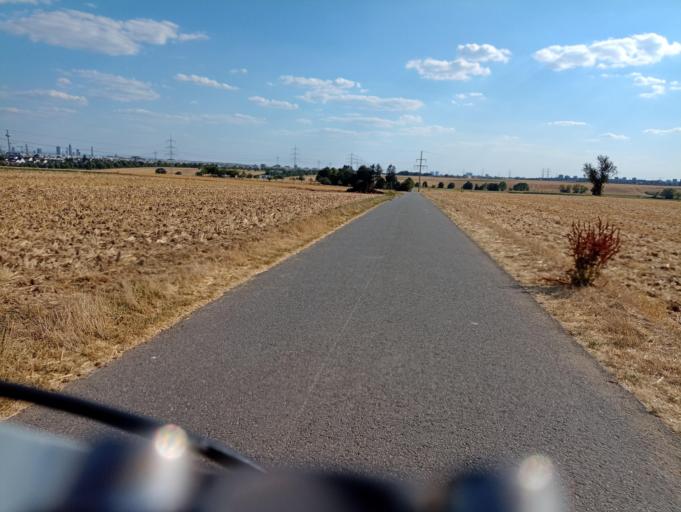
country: DE
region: Hesse
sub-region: Regierungsbezirk Darmstadt
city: Bad Homburg vor der Hoehe
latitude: 50.1976
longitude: 8.6267
